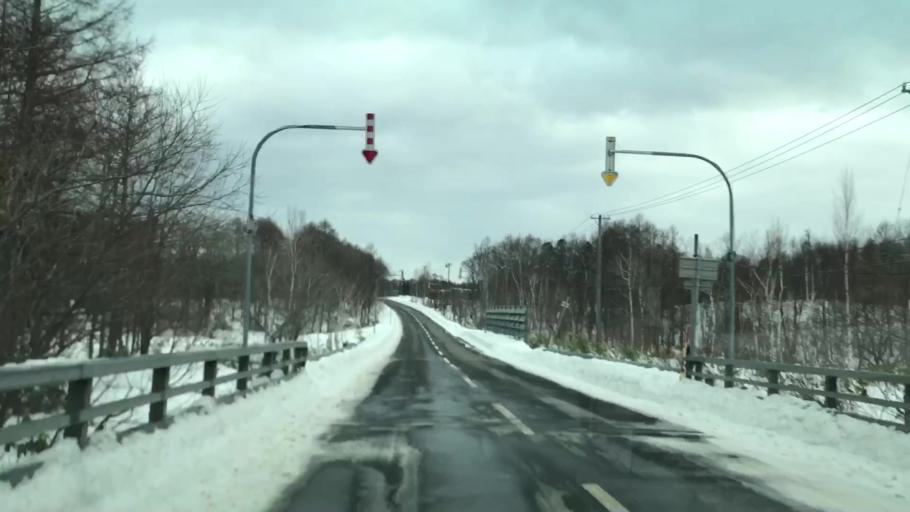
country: JP
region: Hokkaido
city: Yoichi
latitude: 43.3180
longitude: 140.5279
